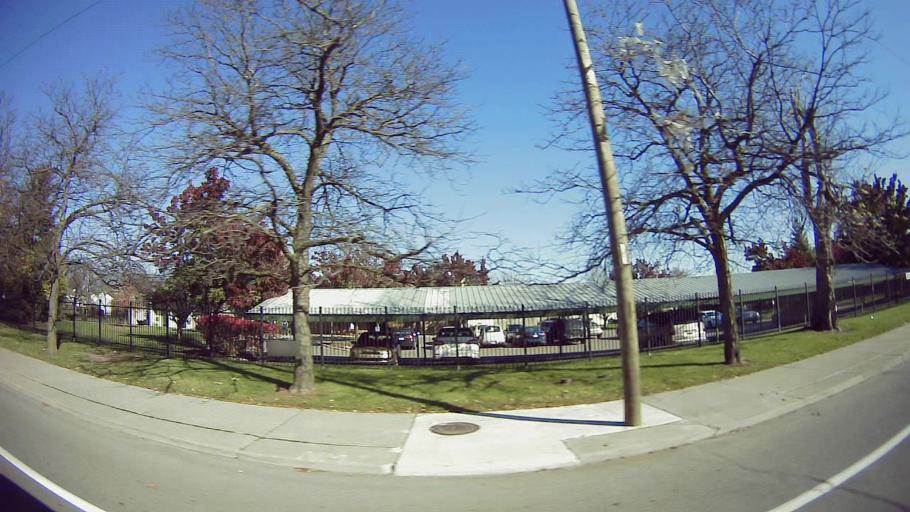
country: US
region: Michigan
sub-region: Wayne County
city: Detroit
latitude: 42.3494
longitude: -83.0771
